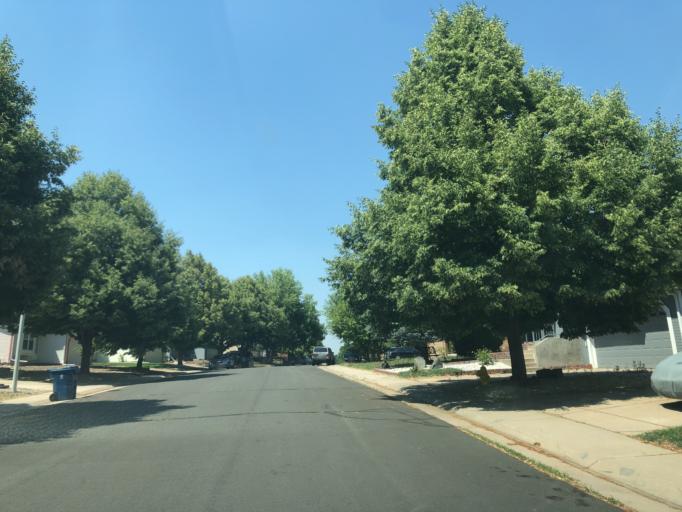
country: US
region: Colorado
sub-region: Arapahoe County
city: Dove Valley
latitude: 39.6328
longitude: -104.7864
